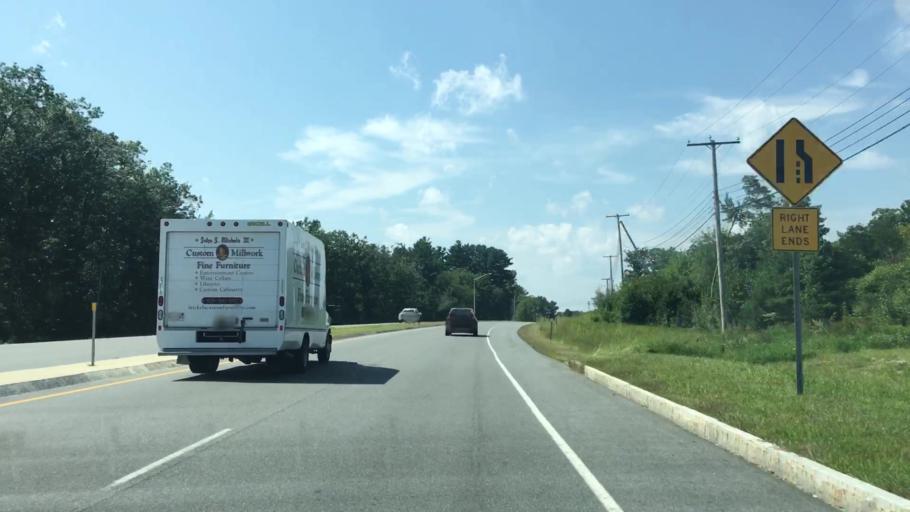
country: US
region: New Hampshire
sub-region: Rockingham County
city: Windham
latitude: 42.8066
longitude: -71.2885
